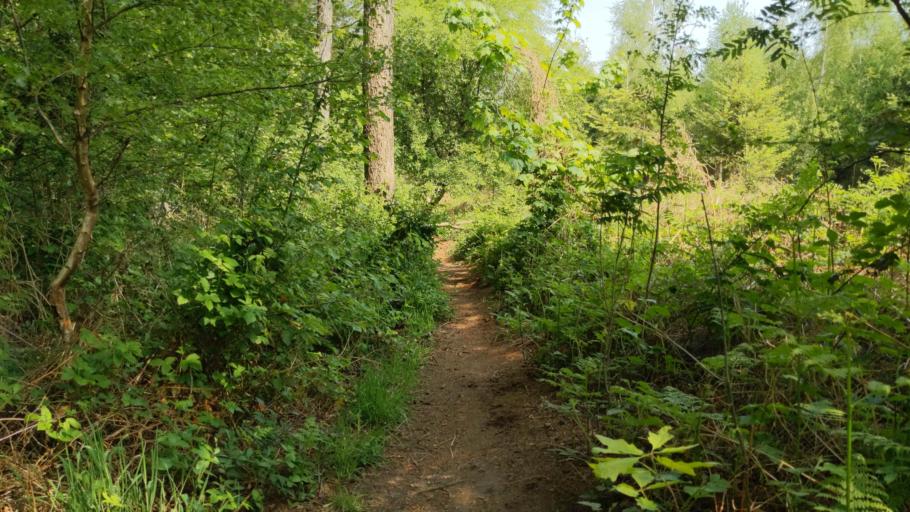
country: DE
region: North Rhine-Westphalia
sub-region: Regierungsbezirk Dusseldorf
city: Meerbusch
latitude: 51.2550
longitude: 6.6499
